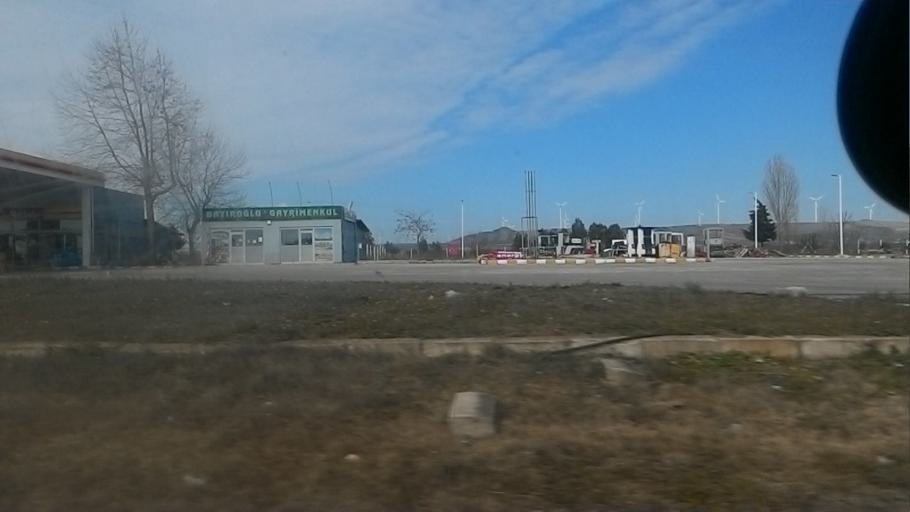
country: TR
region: Istanbul
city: Canta
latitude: 41.0841
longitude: 28.0379
